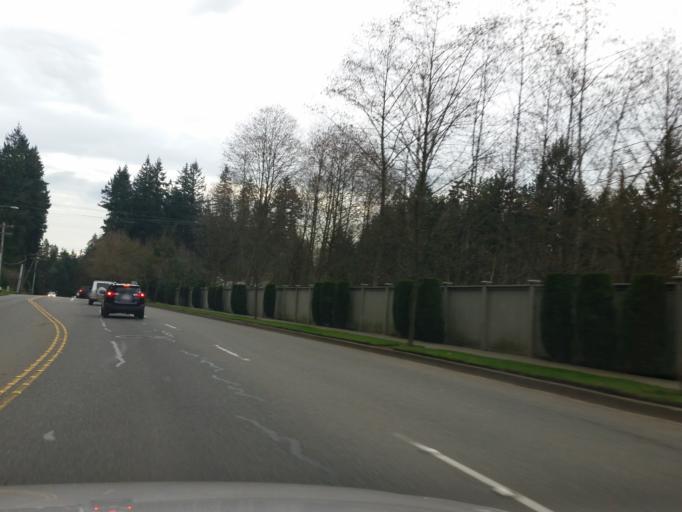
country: US
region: Washington
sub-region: Snohomish County
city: North Creek
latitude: 47.8143
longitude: -122.1903
